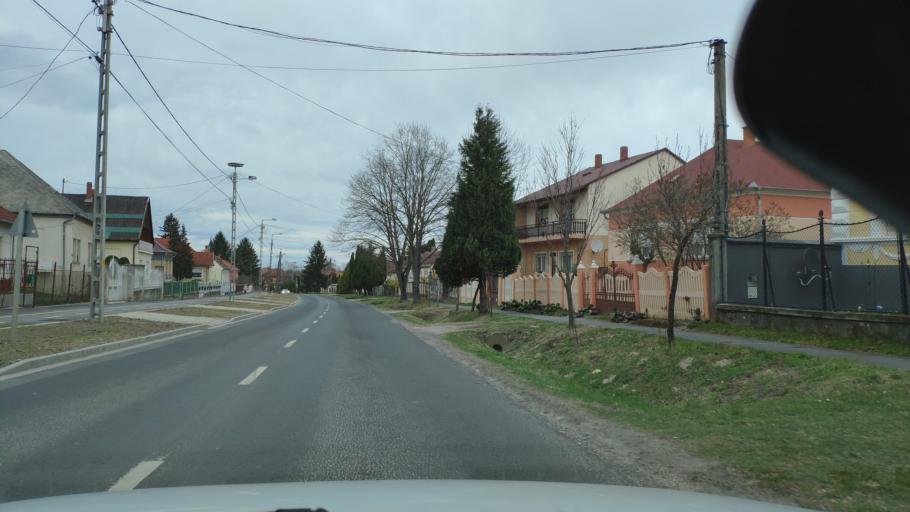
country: HU
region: Zala
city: Zalakomar
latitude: 46.5626
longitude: 17.1238
